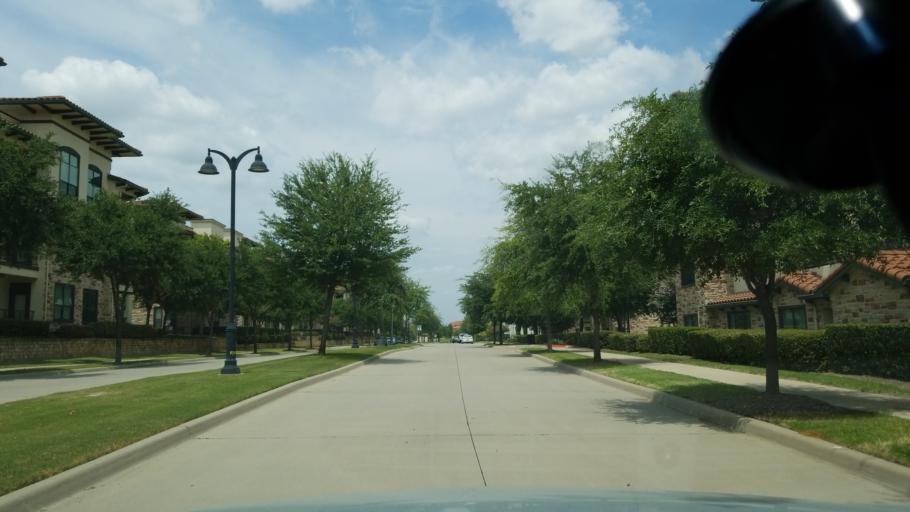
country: US
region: Texas
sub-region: Dallas County
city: Farmers Branch
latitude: 32.8960
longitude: -96.9427
